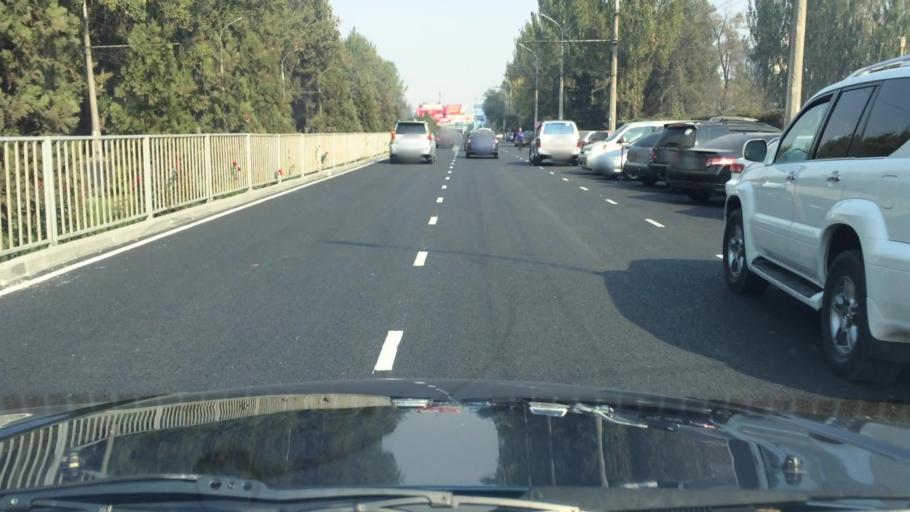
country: KG
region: Chuy
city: Lebedinovka
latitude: 42.8723
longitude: 74.6370
